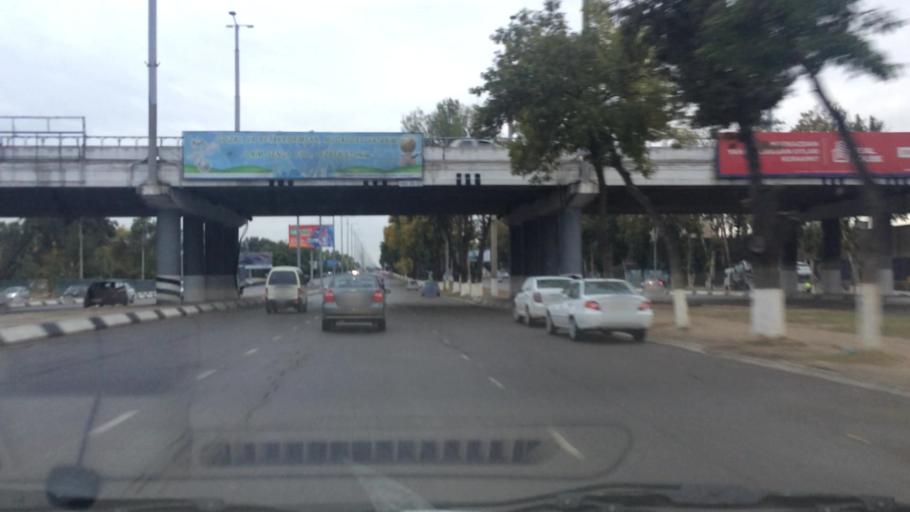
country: UZ
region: Toshkent Shahri
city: Tashkent
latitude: 41.2566
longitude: 69.1931
